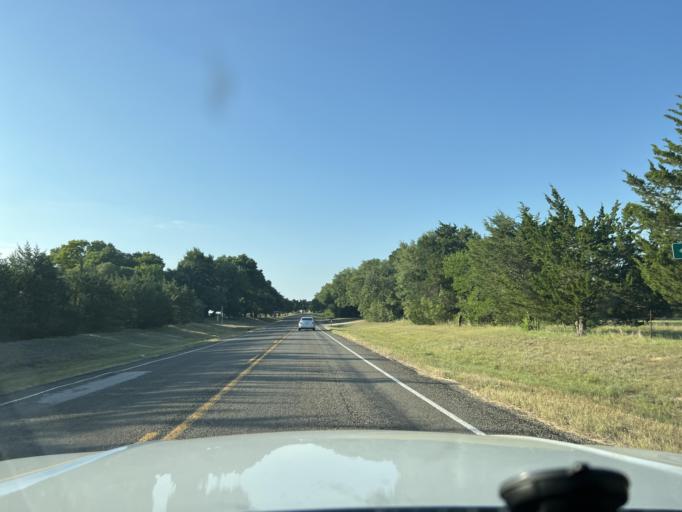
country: US
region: Texas
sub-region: Washington County
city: Brenham
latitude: 30.2061
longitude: -96.3934
